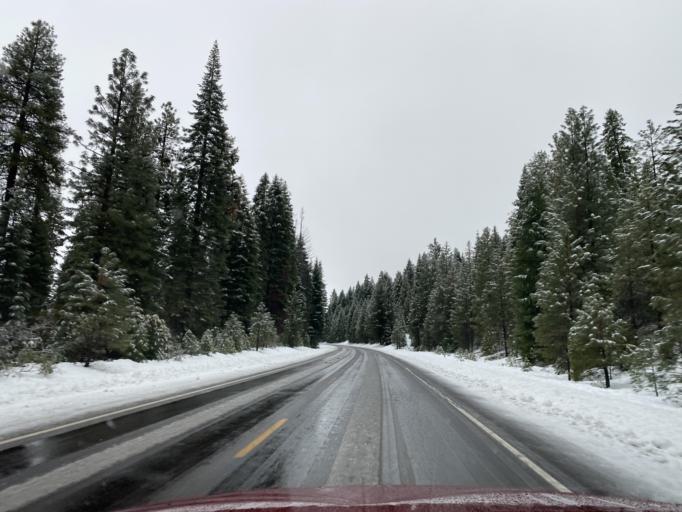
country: US
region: Oregon
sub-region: Klamath County
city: Klamath Falls
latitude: 42.5380
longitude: -122.0902
